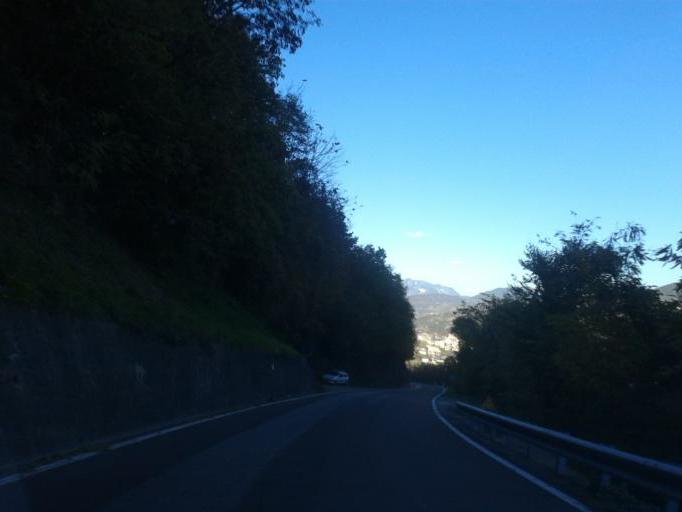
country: IT
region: Trentino-Alto Adige
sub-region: Provincia di Trento
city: Trento
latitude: 46.0764
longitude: 11.0980
